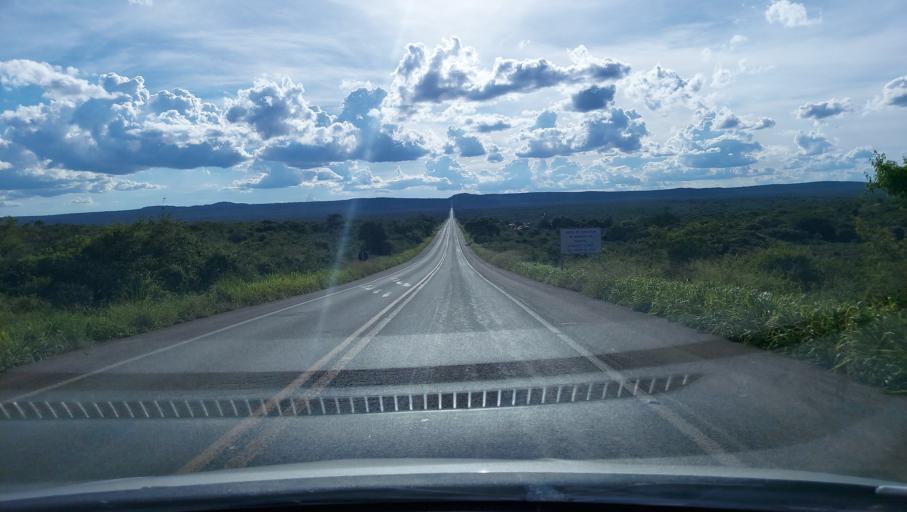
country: BR
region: Bahia
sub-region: Seabra
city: Seabra
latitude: -12.3960
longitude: -41.9309
